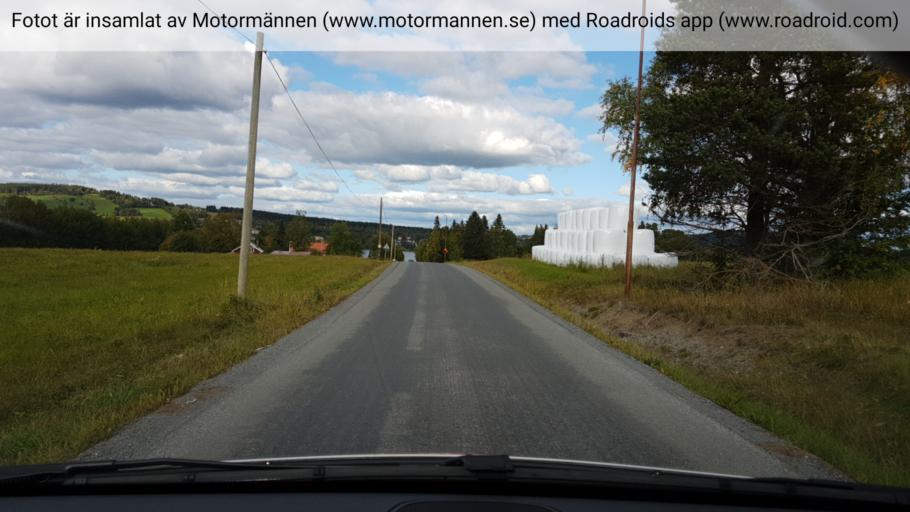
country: SE
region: Jaemtland
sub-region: OEstersunds Kommun
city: Ostersund
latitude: 63.1495
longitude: 14.5455
